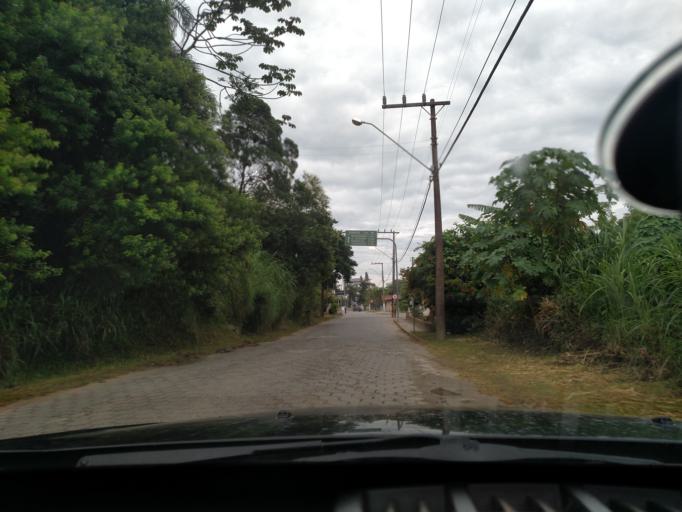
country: BR
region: Santa Catarina
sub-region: Porto Belo
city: Porto Belo
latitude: -27.1781
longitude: -48.5223
